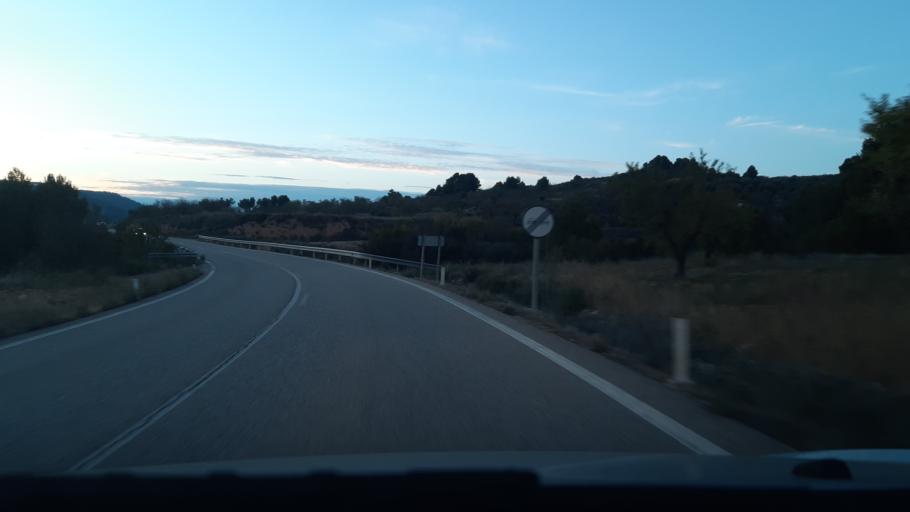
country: ES
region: Aragon
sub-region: Provincia de Teruel
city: Valderrobres
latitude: 40.8634
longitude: 0.1694
